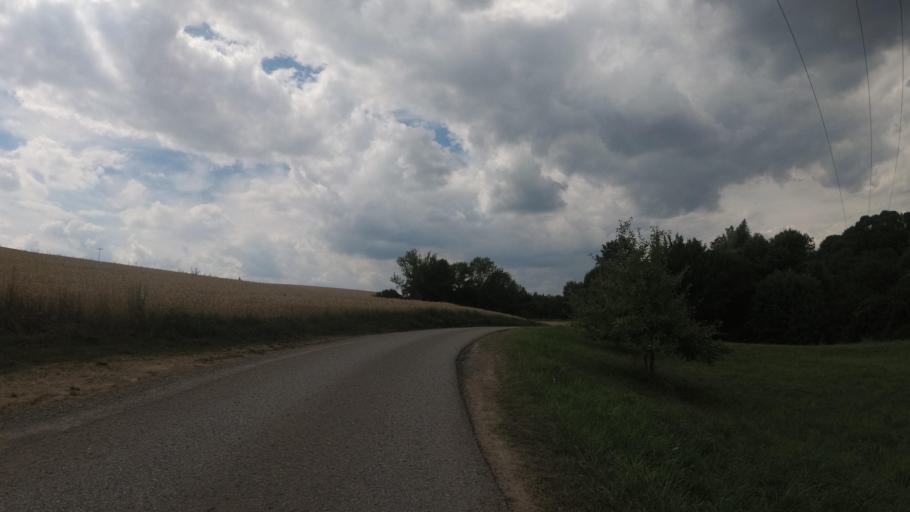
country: DE
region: Baden-Wuerttemberg
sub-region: Regierungsbezirk Stuttgart
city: Neudenau
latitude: 49.2765
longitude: 9.2714
